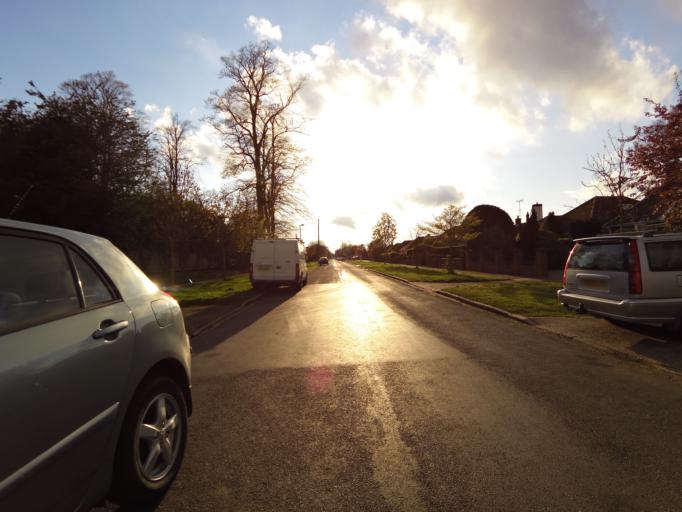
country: GB
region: England
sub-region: Suffolk
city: Ipswich
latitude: 52.0722
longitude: 1.1702
